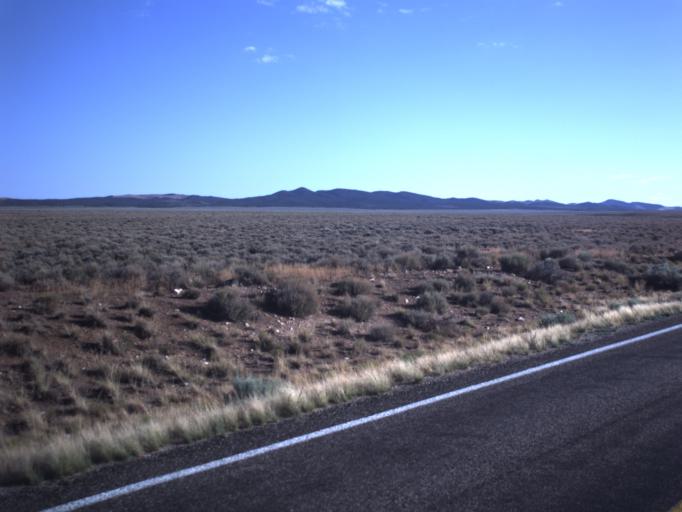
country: US
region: Utah
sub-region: Iron County
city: Enoch
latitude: 37.9345
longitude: -113.0263
